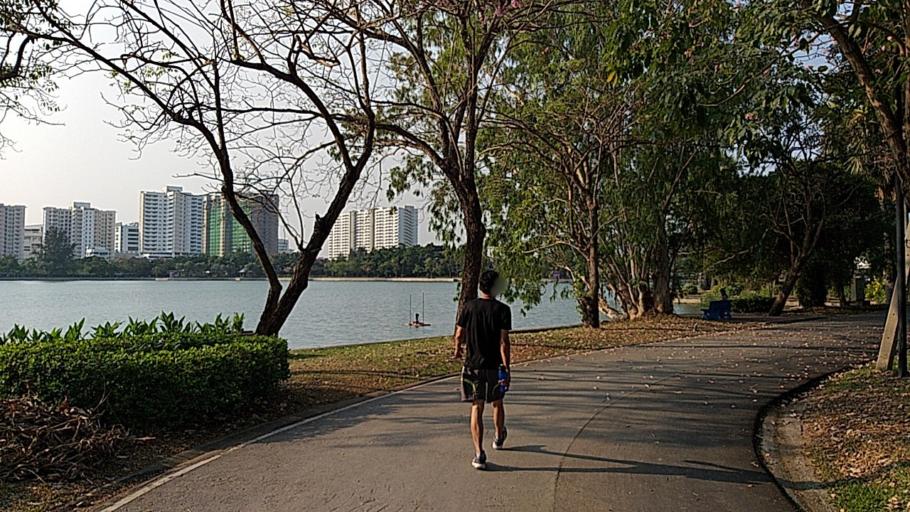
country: TH
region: Bangkok
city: Don Mueang
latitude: 13.9296
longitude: 100.5536
